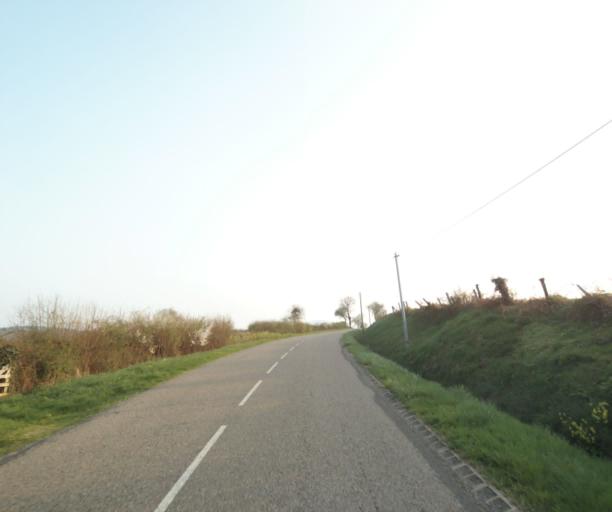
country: FR
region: Bourgogne
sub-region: Departement de Saone-et-Loire
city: Charolles
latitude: 46.4498
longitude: 4.4293
